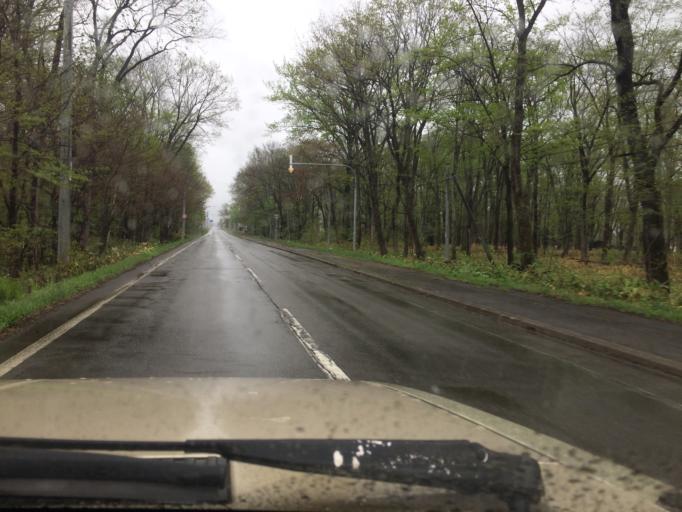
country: JP
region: Hokkaido
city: Obihiro
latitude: 42.8269
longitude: 142.9904
